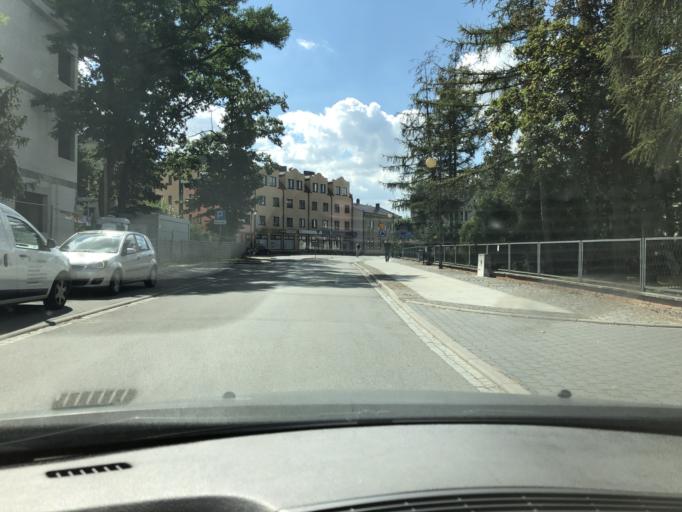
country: PL
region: Lodz Voivodeship
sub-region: Powiat wieruszowski
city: Wieruszow
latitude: 51.2958
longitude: 18.1580
